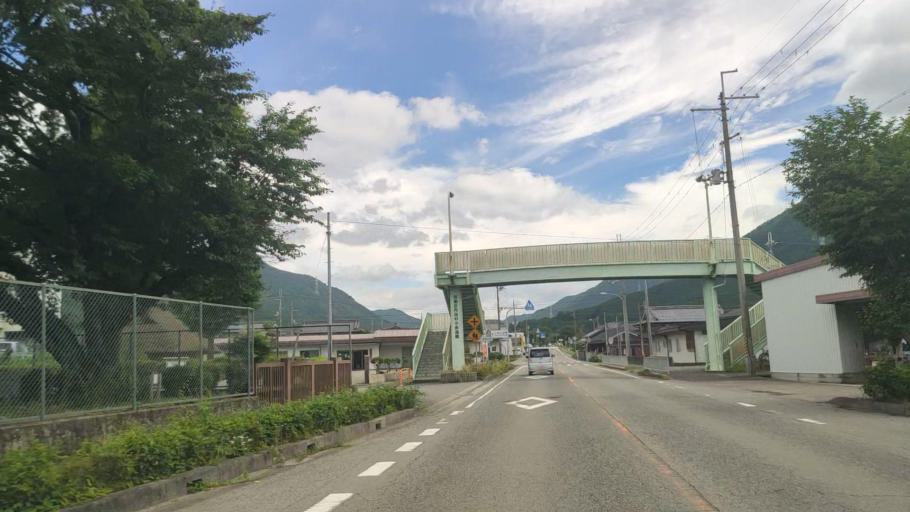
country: JP
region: Hyogo
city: Nishiwaki
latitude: 35.1365
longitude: 134.9249
